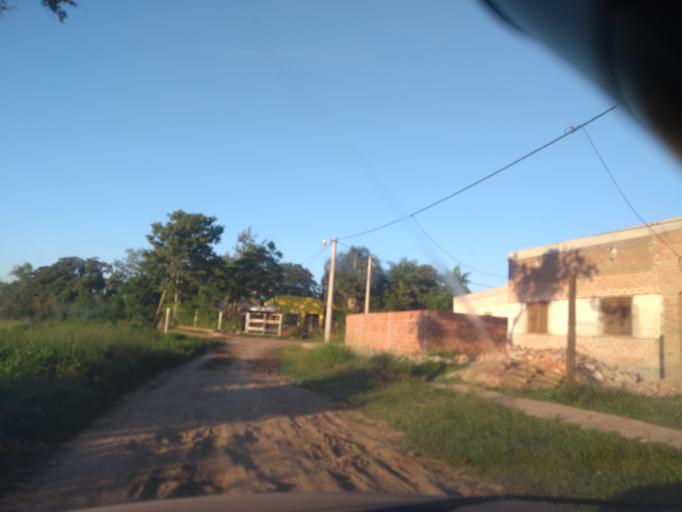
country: AR
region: Chaco
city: Resistencia
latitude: -27.4587
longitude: -58.9684
